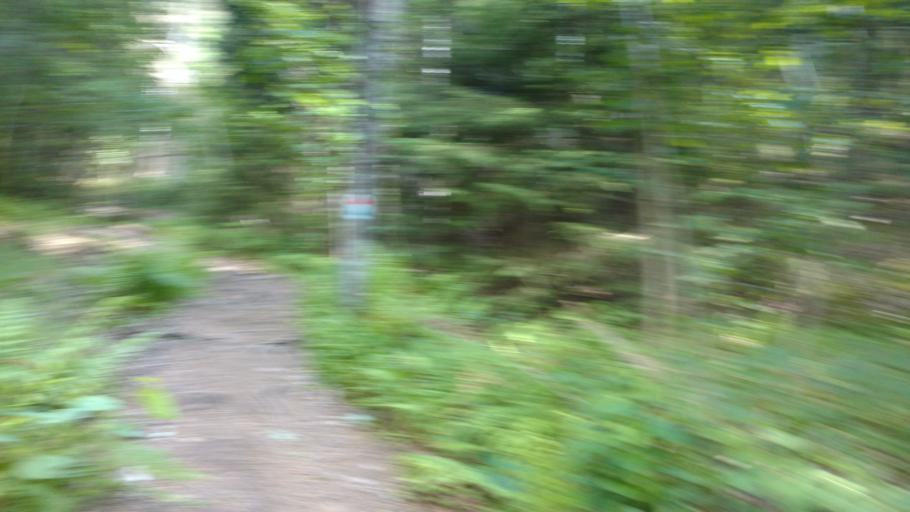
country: FI
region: Uusimaa
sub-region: Raaseporin
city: Pohja
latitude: 60.1100
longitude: 23.5492
